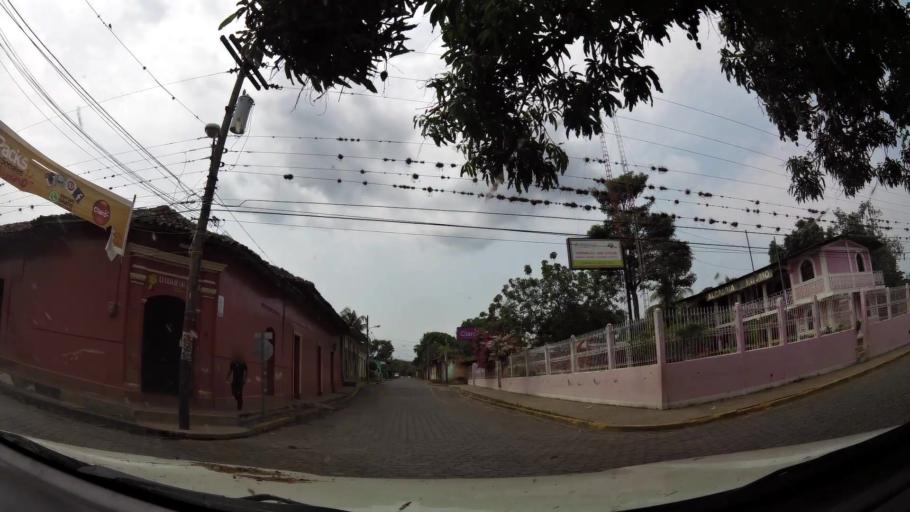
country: NI
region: Granada
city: Diriomo
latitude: 11.8746
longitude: -86.0522
